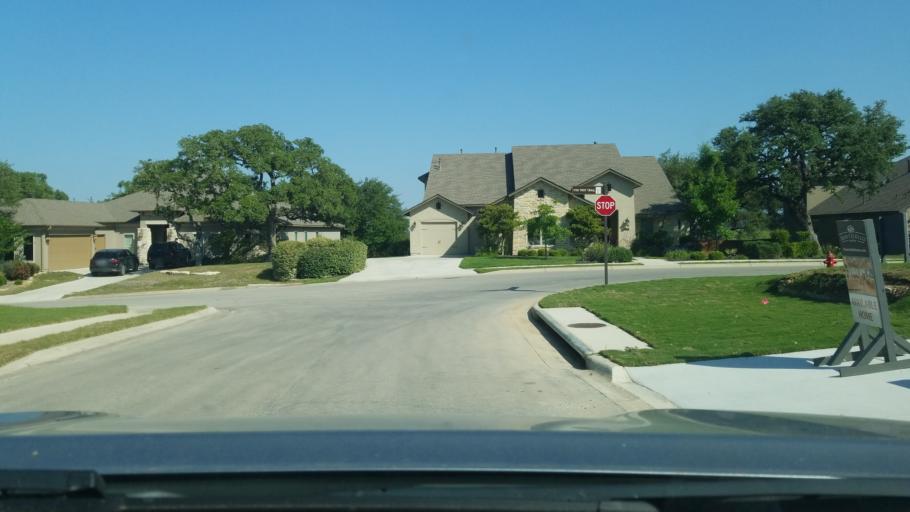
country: US
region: Texas
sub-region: Comal County
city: Bulverde
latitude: 29.7602
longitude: -98.4200
